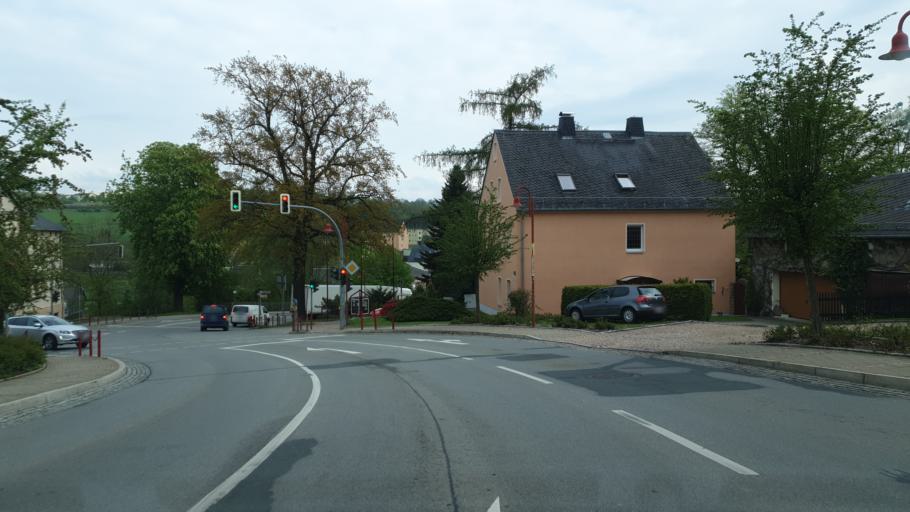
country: DE
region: Saxony
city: Lugau
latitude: 50.7227
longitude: 12.7551
